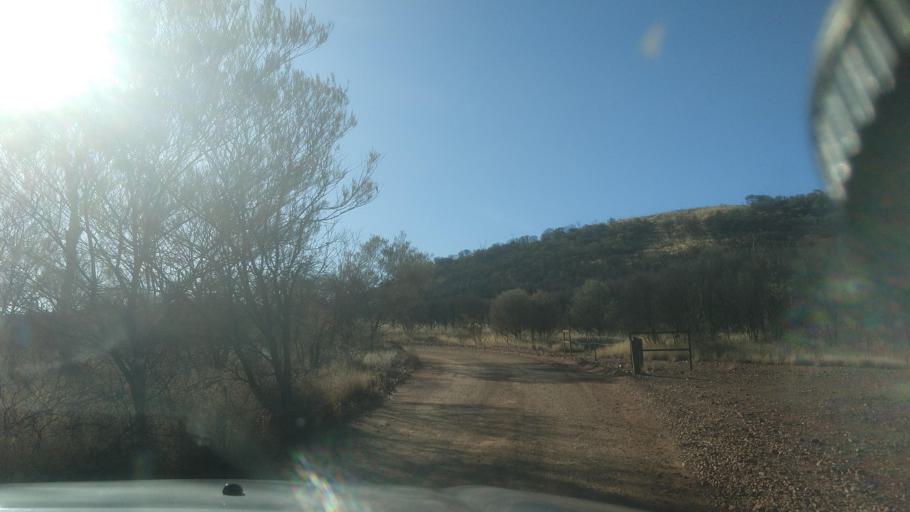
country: AU
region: Northern Territory
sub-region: Alice Springs
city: Alice Springs
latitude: -23.7490
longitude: 132.9153
